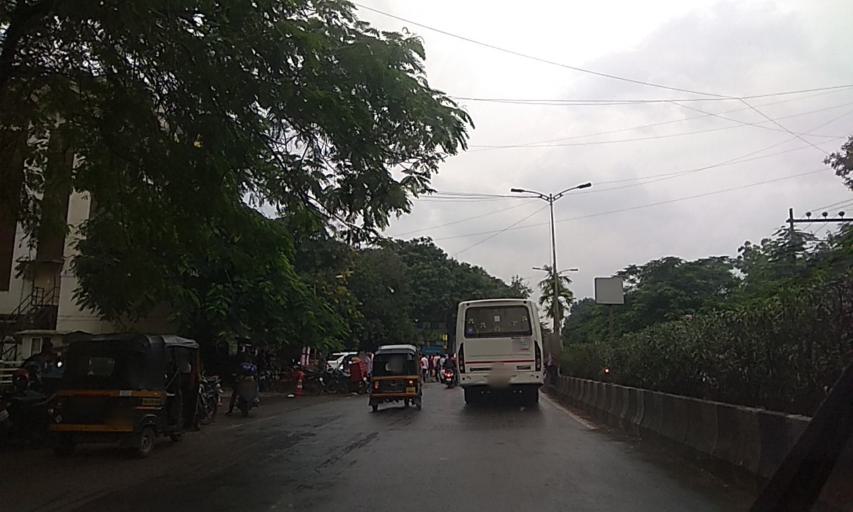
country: IN
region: Maharashtra
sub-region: Pune Division
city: Lohogaon
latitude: 18.5632
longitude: 73.9180
